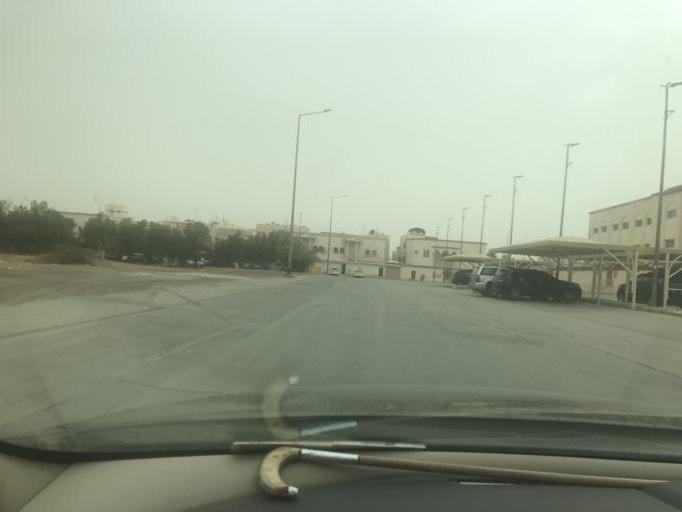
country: SA
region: Ar Riyad
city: Riyadh
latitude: 24.7284
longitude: 46.7902
